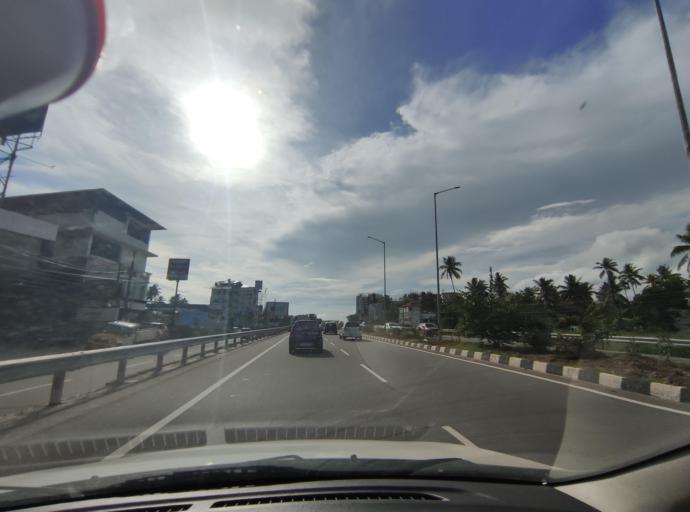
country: IN
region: Kerala
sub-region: Thiruvananthapuram
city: Thiruvananthapuram
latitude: 8.5071
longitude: 76.9073
